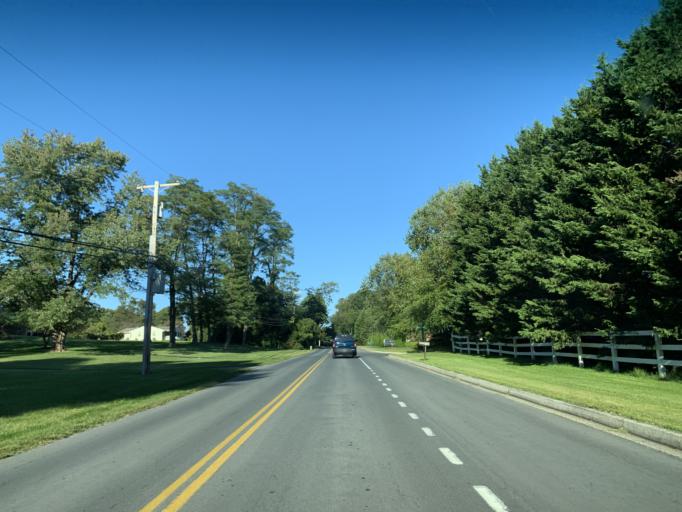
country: US
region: Maryland
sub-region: Harford County
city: Jarrettsville
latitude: 39.5769
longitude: -76.4625
